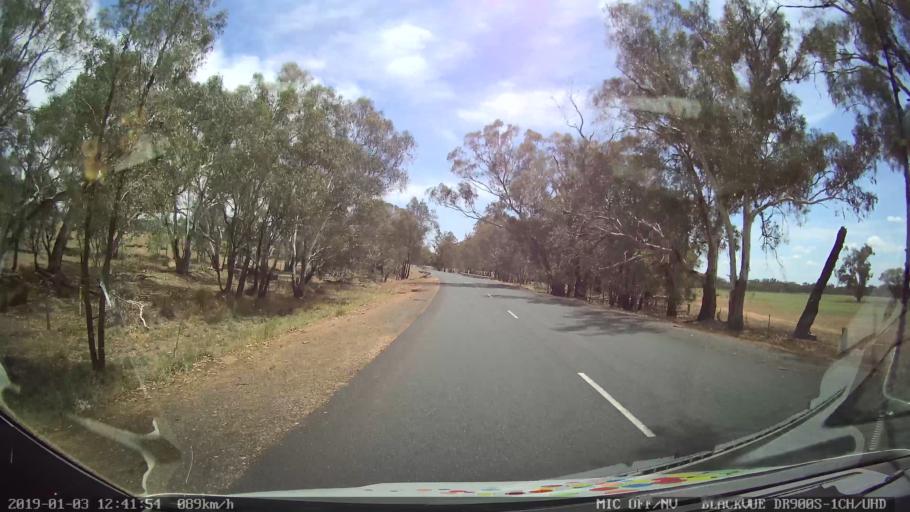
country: AU
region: New South Wales
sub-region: Weddin
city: Grenfell
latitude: -33.7935
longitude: 148.2151
